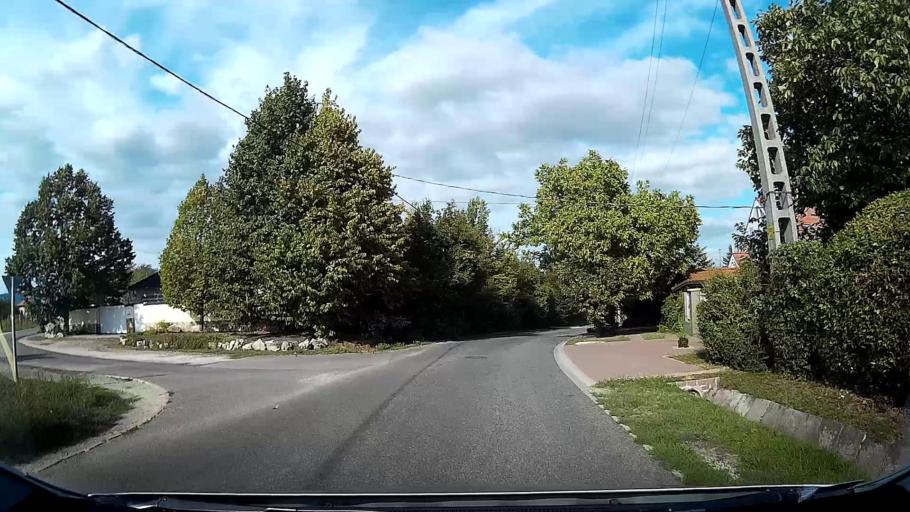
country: HU
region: Pest
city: Pomaz
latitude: 47.6357
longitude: 19.0214
